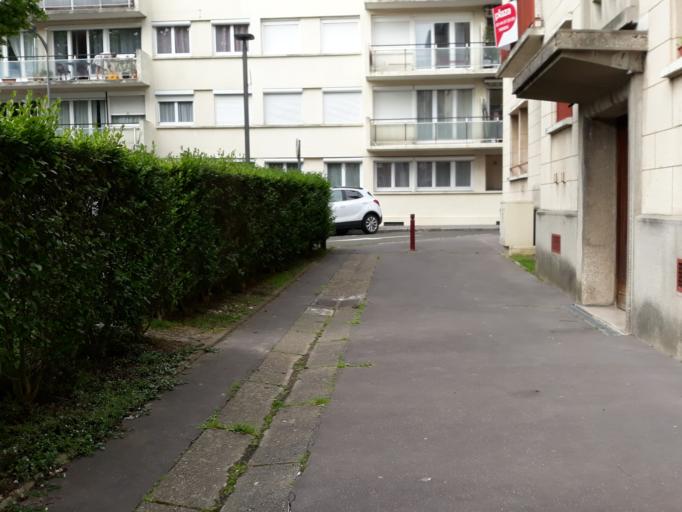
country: FR
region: Picardie
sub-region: Departement de l'Oise
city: Beauvais
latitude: 49.4297
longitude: 2.0857
